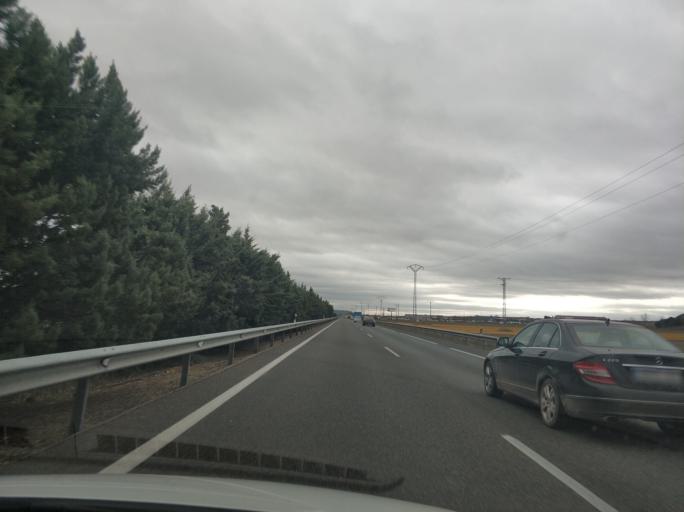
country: ES
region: Castille and Leon
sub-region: Provincia de Valladolid
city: Cubillas de Santa Marta
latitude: 41.8265
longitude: -4.5747
